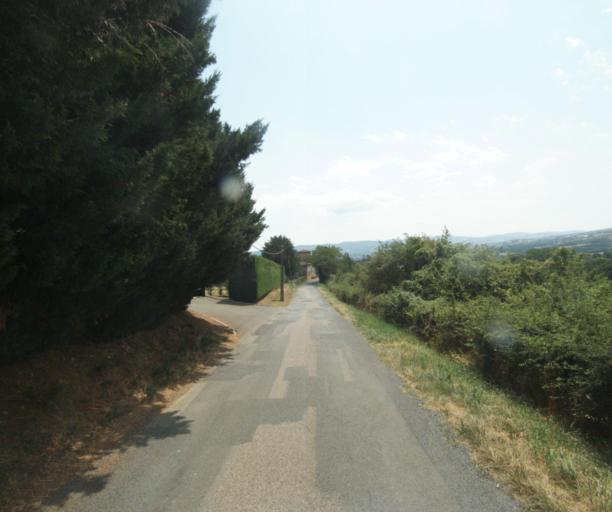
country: FR
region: Rhone-Alpes
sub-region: Departement du Rhone
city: Saint-Germain-Nuelles
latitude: 45.8628
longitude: 4.5991
